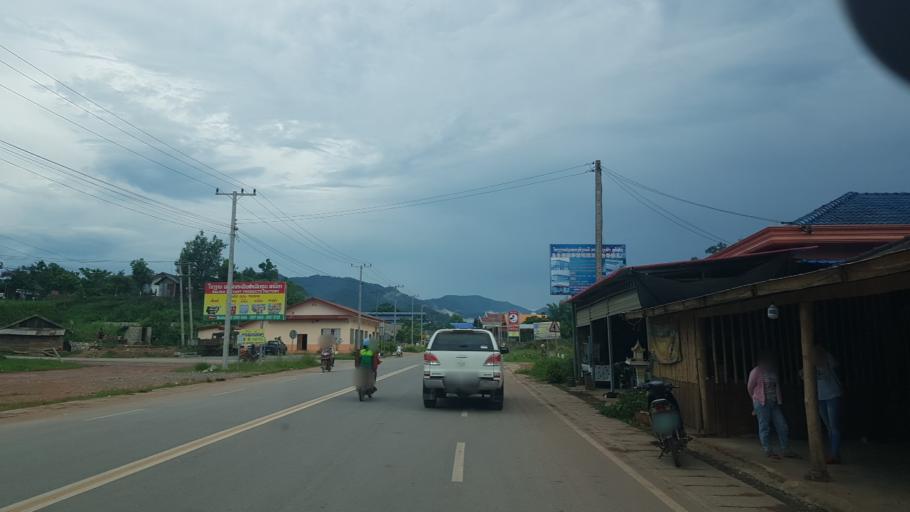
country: LA
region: Oudomxai
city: Muang Xay
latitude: 20.6541
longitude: 101.9770
